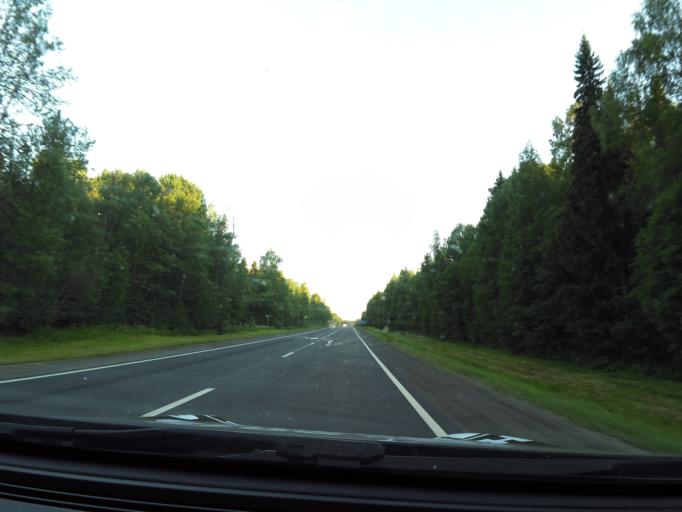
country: RU
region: Jaroslavl
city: Prechistoye
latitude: 58.5194
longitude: 40.3472
